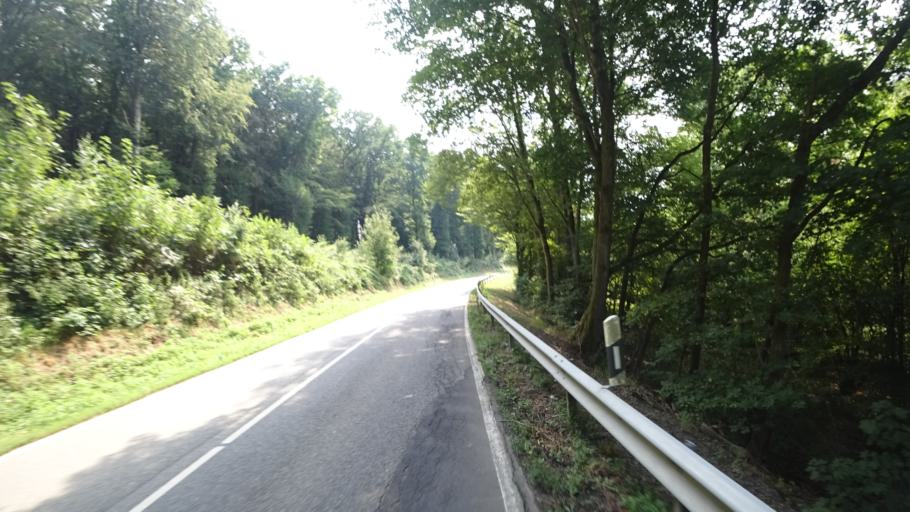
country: DE
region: Rheinland-Pfalz
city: Hohr-Grenzhausen
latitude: 50.4288
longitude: 7.6508
